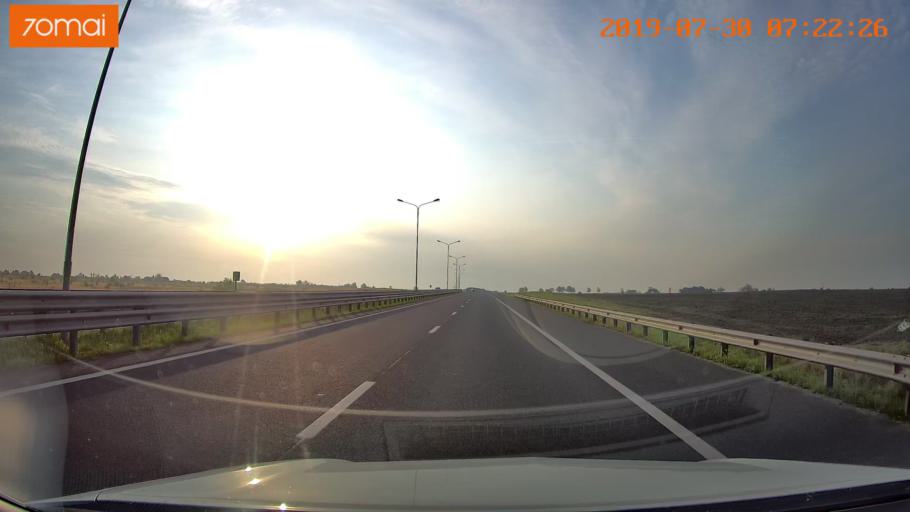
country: RU
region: Kaliningrad
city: Bol'shoe Isakovo
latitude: 54.6925
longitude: 20.7557
